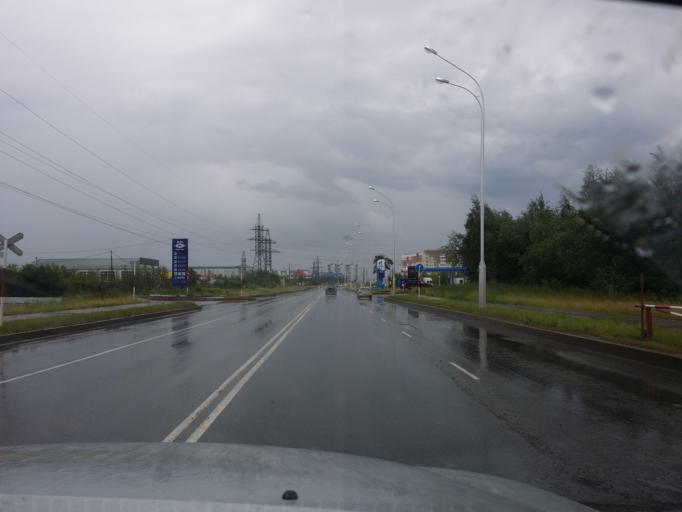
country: RU
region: Khanty-Mansiyskiy Avtonomnyy Okrug
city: Nizhnevartovsk
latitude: 60.9623
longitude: 76.5559
